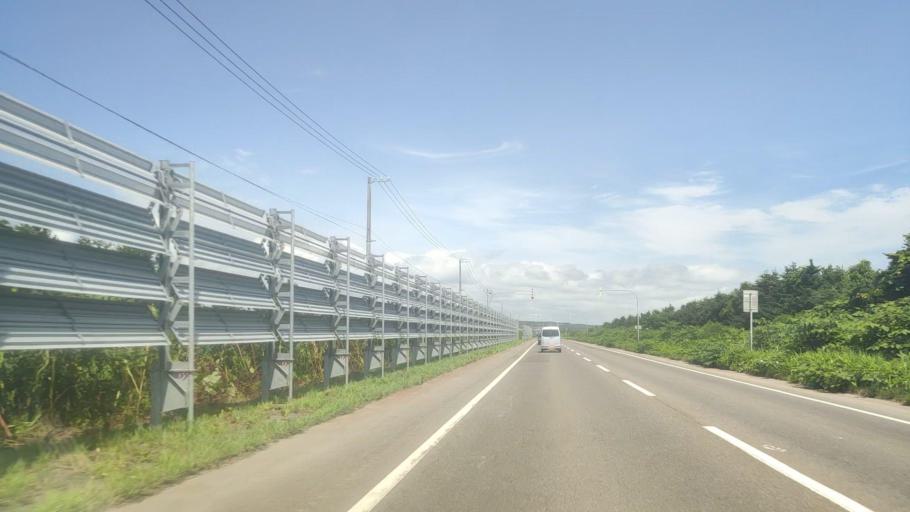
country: JP
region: Hokkaido
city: Nanae
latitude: 42.2960
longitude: 140.2718
